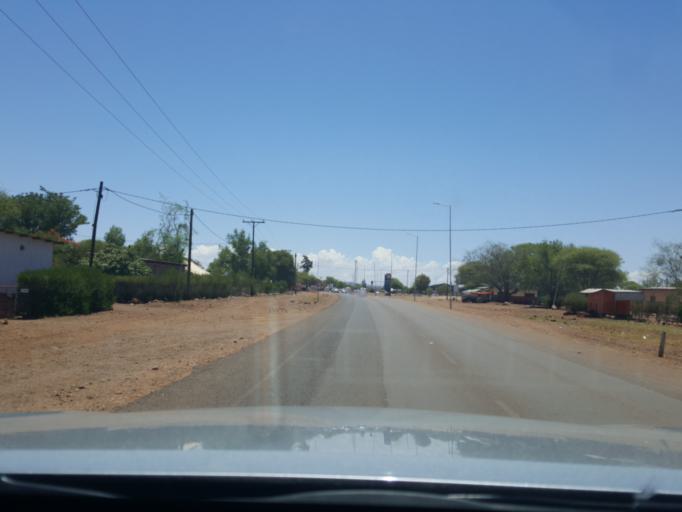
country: BW
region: South East
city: Ramotswa
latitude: -24.8664
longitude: 25.8662
